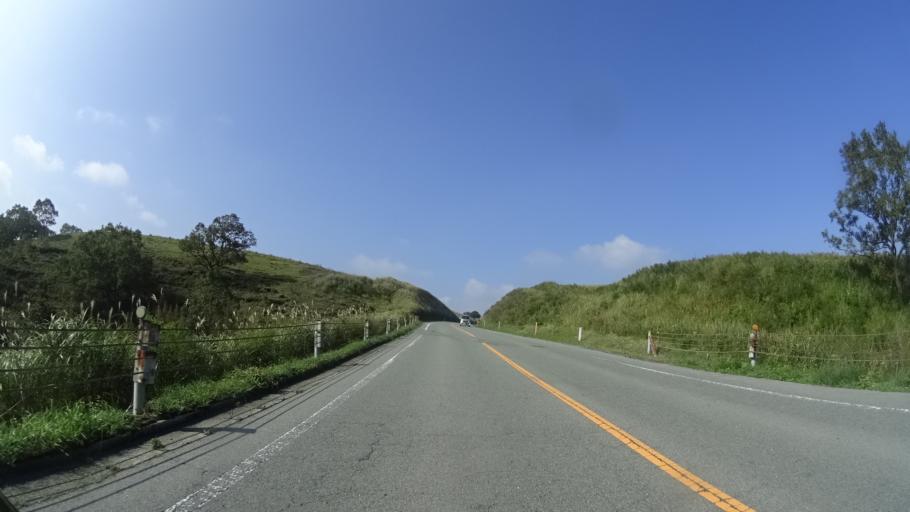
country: JP
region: Kumamoto
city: Aso
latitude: 33.0165
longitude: 131.0687
